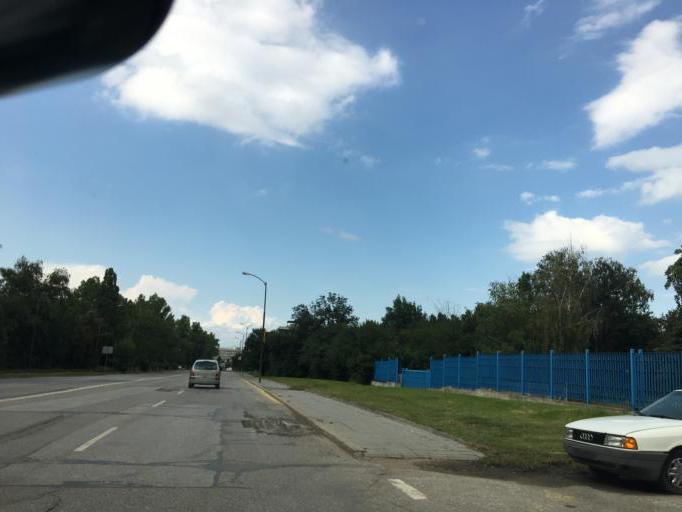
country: BG
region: Sofia-Capital
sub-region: Stolichna Obshtina
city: Sofia
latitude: 42.6581
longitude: 23.3591
